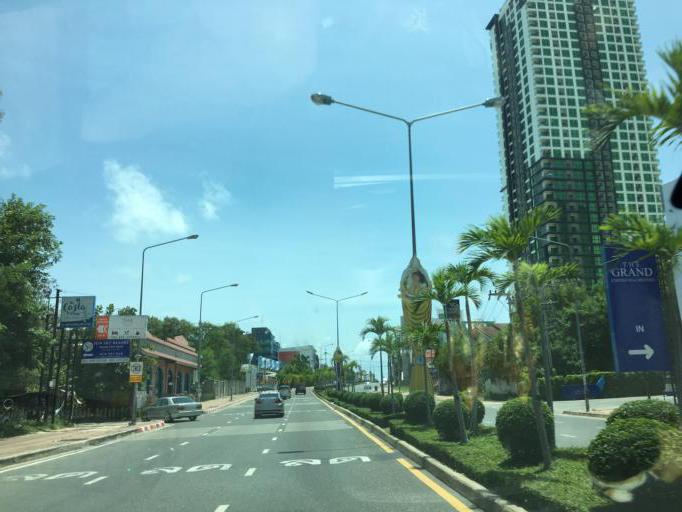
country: TH
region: Chon Buri
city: Phatthaya
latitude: 12.8921
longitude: 100.8779
